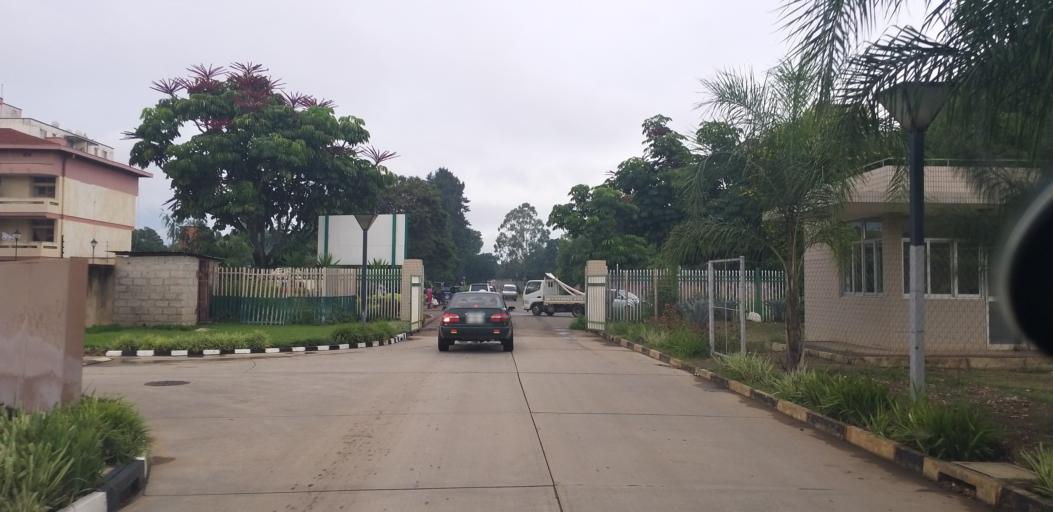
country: ZM
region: Lusaka
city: Lusaka
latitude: -15.4215
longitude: 28.2919
